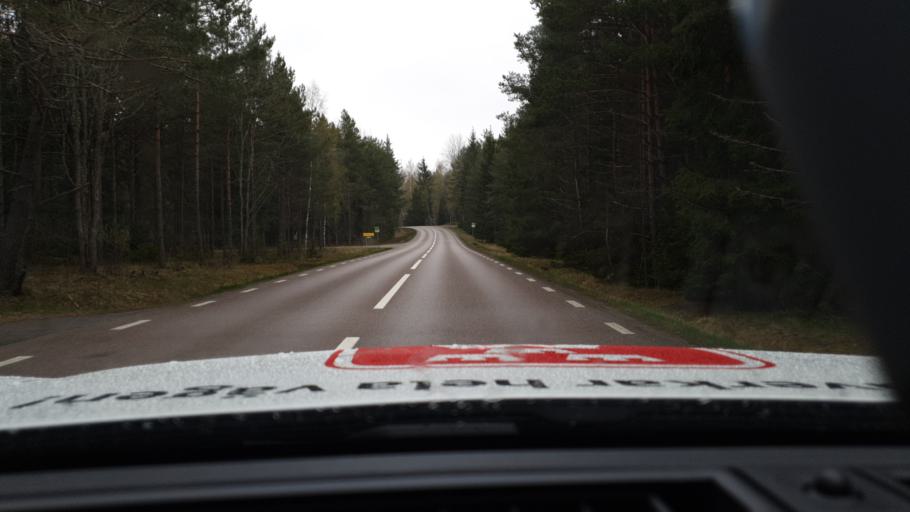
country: SE
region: Soedermanland
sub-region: Strangnas Kommun
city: Mariefred
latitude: 59.1765
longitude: 17.1881
